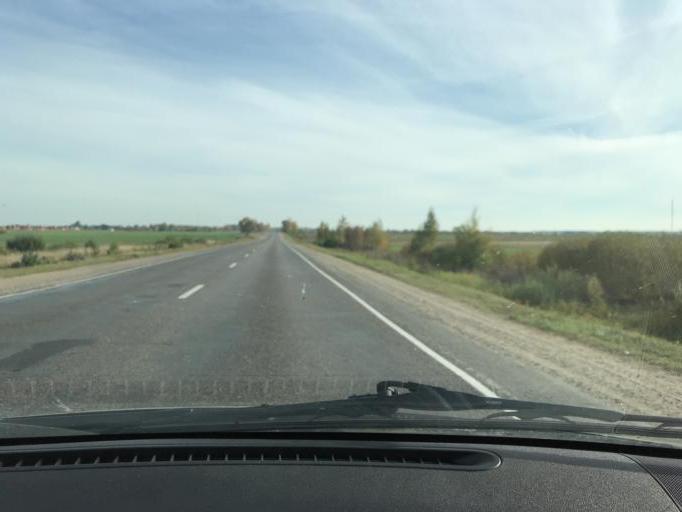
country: BY
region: Brest
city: Asnyezhytsy
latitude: 52.2085
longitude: 26.0511
